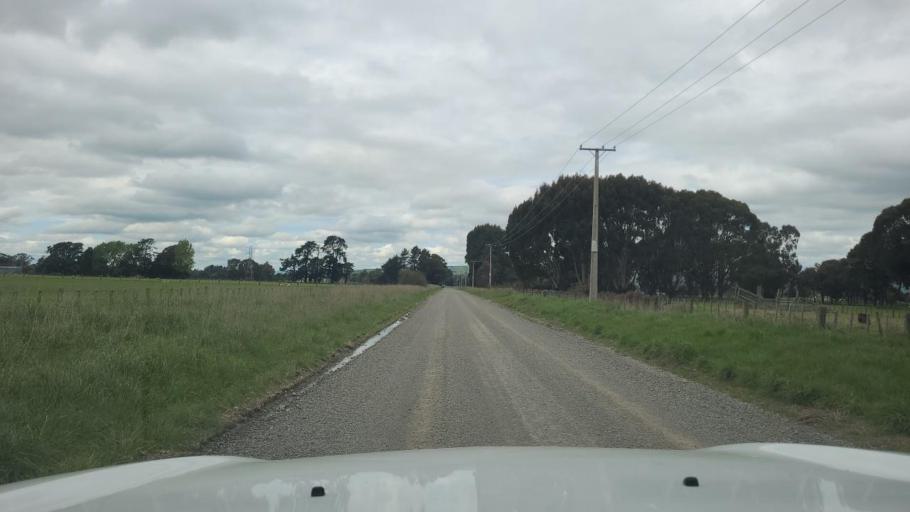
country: NZ
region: Wellington
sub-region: Masterton District
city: Masterton
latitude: -41.1191
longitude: 175.4292
